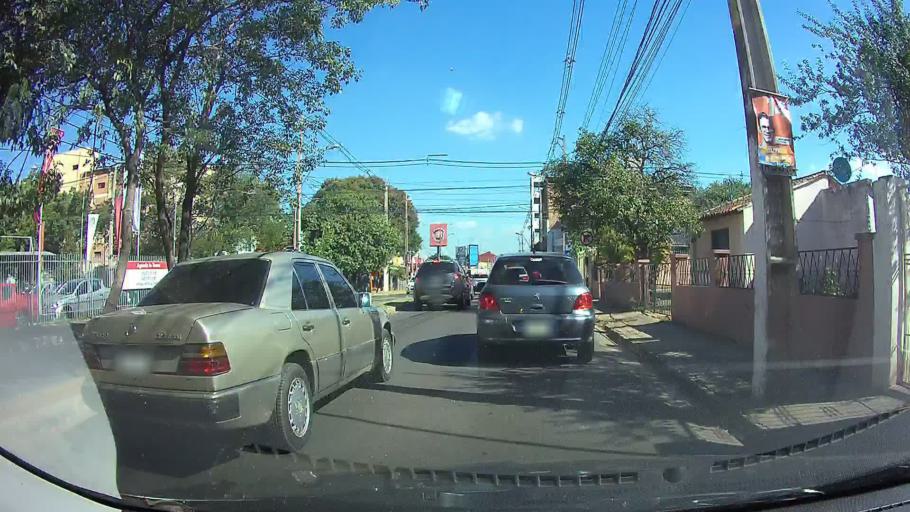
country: PY
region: Central
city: Lambare
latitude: -25.3151
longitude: -57.5731
